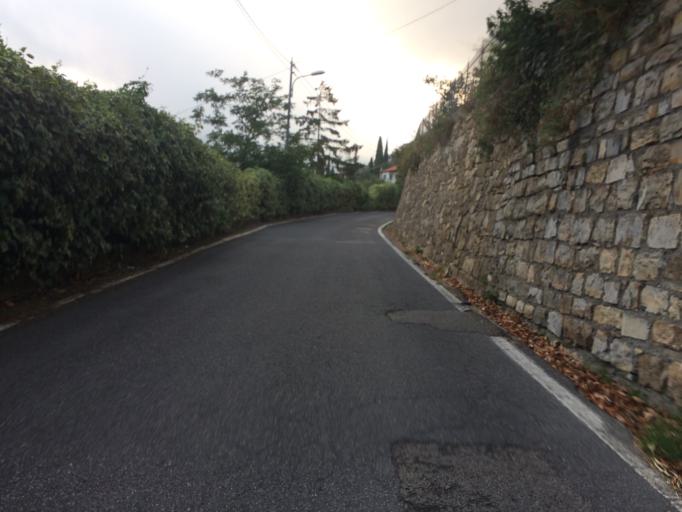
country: IT
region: Liguria
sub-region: Provincia di Imperia
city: San Remo
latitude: 43.8433
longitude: 7.7446
